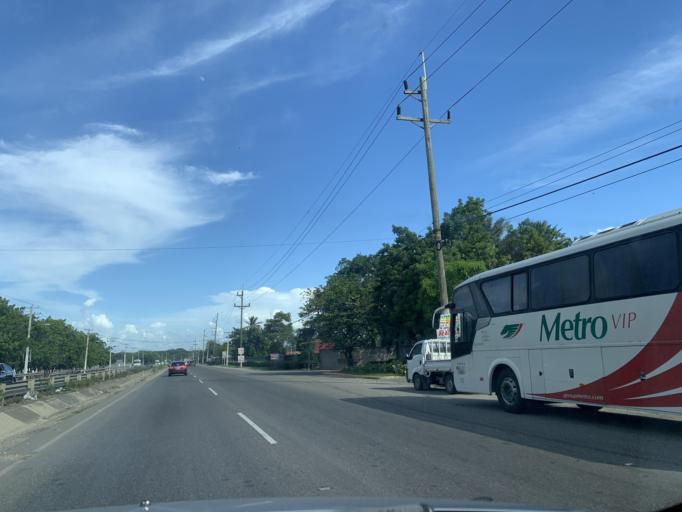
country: DO
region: Santiago
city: Villa Gonzalez
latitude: 19.5290
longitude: -70.7756
